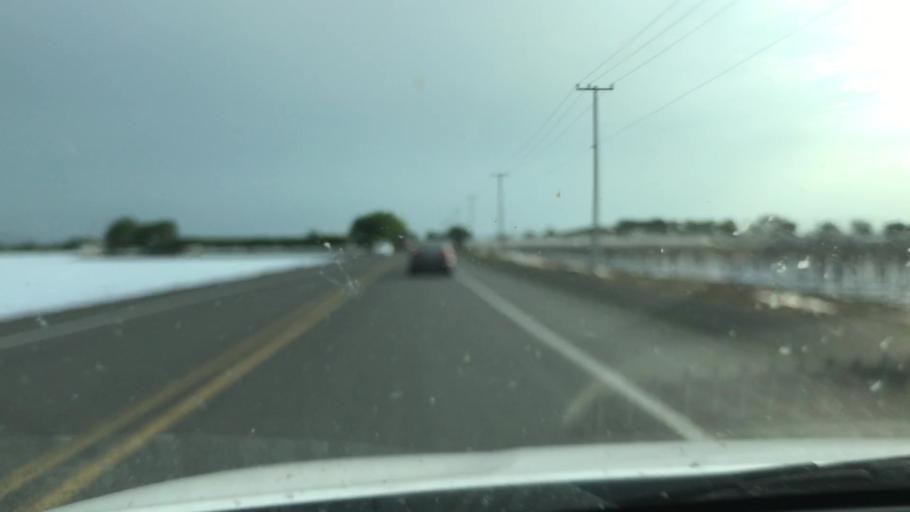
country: MX
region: Michoacan
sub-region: Yurecuaro
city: Yurecuaro
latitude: 20.3217
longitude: -102.2887
